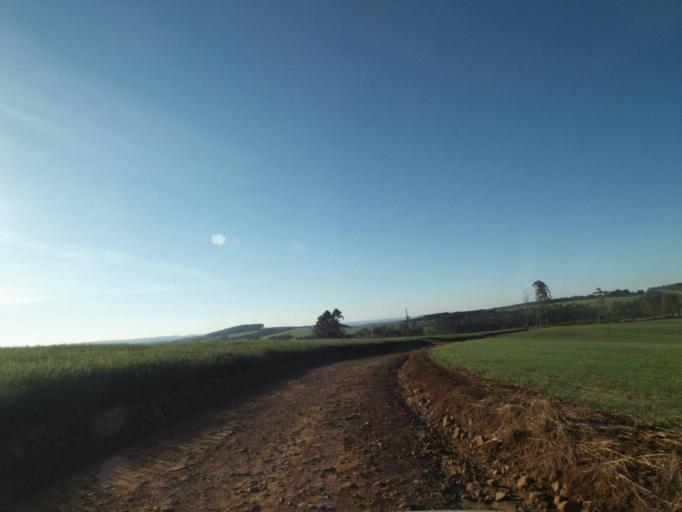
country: BR
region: Parana
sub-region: Telemaco Borba
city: Telemaco Borba
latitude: -24.4834
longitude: -50.5941
